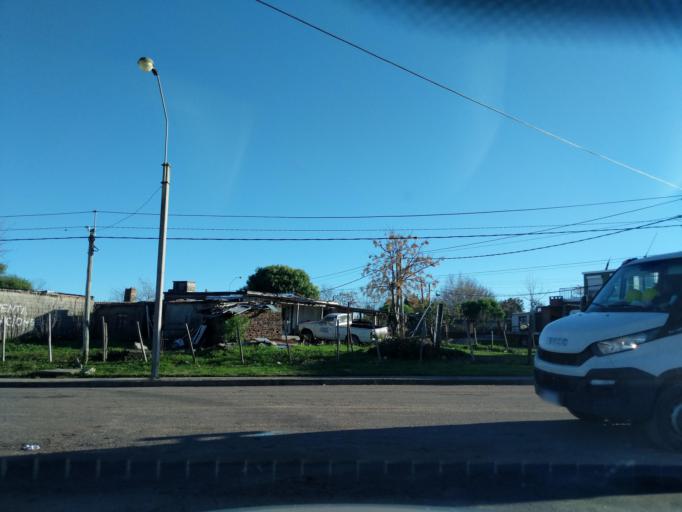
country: UY
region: Florida
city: Florida
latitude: -34.0983
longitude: -56.2390
